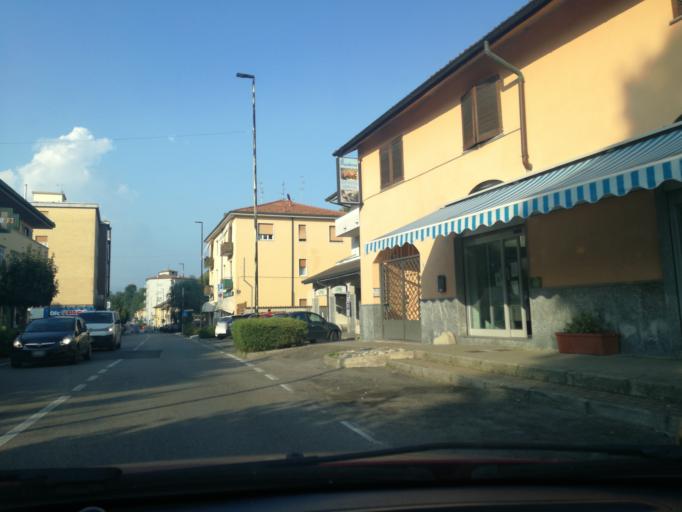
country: IT
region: Lombardy
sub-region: Provincia di Monza e Brianza
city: Usmate-Velate
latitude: 45.6510
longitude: 9.3630
